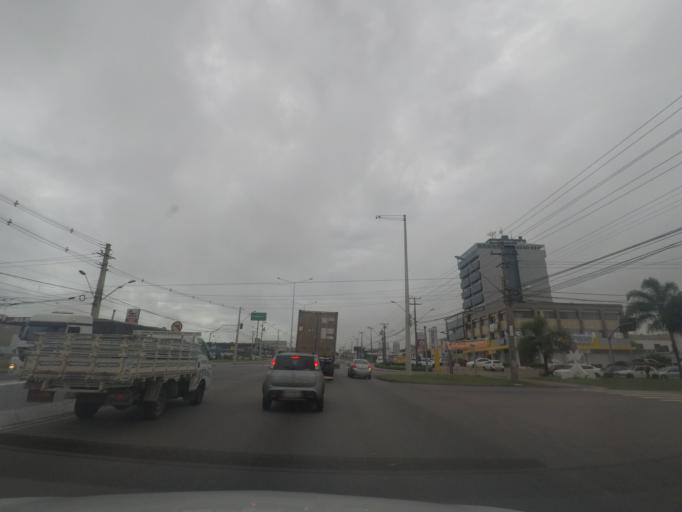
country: BR
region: Parana
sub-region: Pinhais
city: Pinhais
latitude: -25.4324
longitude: -49.1937
